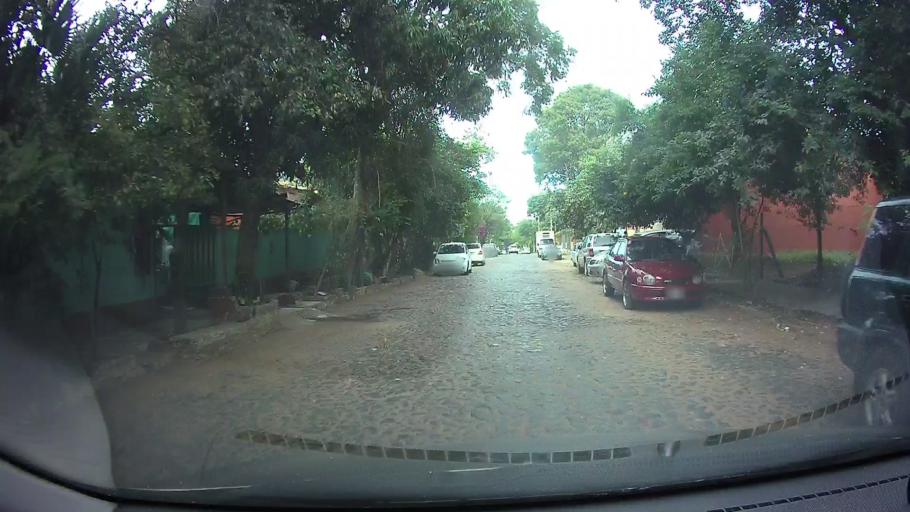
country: PY
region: Central
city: Lambare
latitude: -25.3196
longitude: -57.5983
